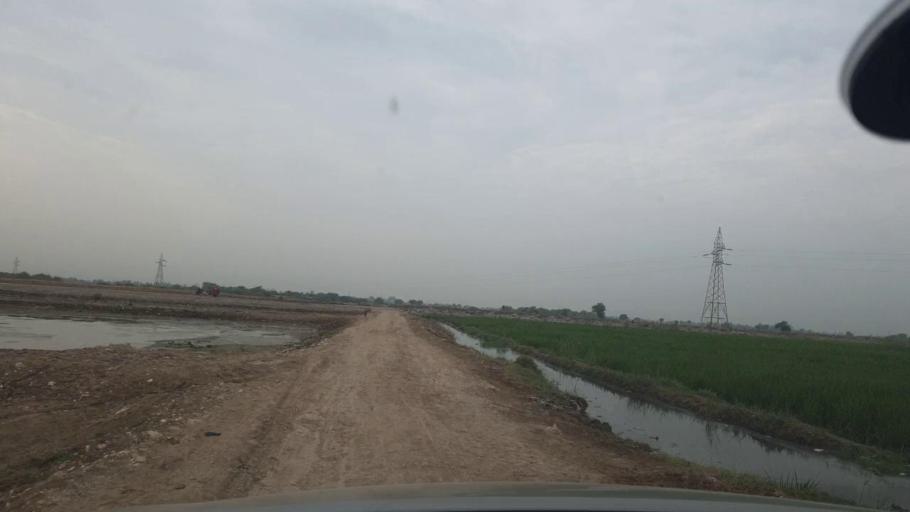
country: PK
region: Sindh
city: Jacobabad
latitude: 28.2863
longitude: 68.4169
